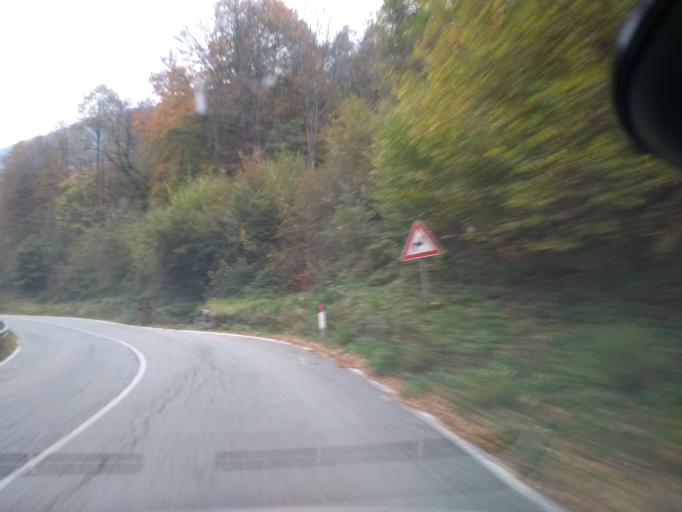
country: IT
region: Piedmont
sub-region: Provincia di Torino
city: Ceres
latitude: 45.3213
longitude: 7.3970
